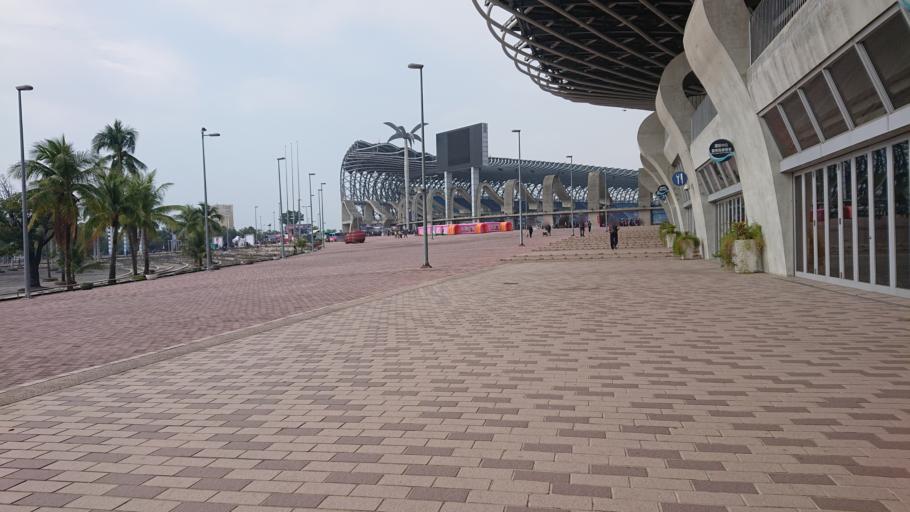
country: TW
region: Kaohsiung
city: Kaohsiung
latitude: 22.7013
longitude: 120.2962
